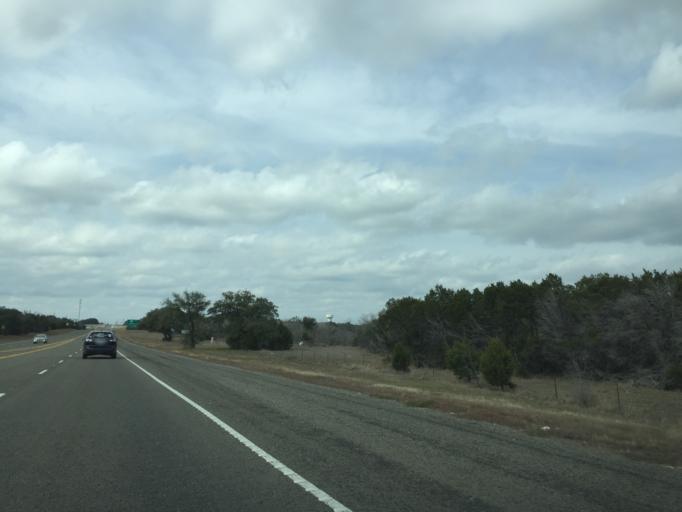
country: US
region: Texas
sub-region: Burnet County
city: Meadowlakes
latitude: 30.5063
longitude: -98.2844
